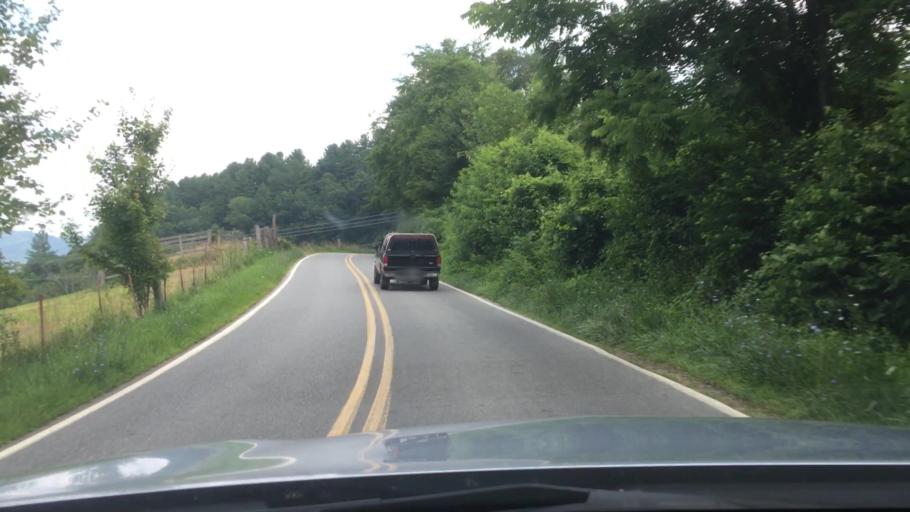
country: US
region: North Carolina
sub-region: Yancey County
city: Burnsville
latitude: 35.9023
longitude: -82.3579
